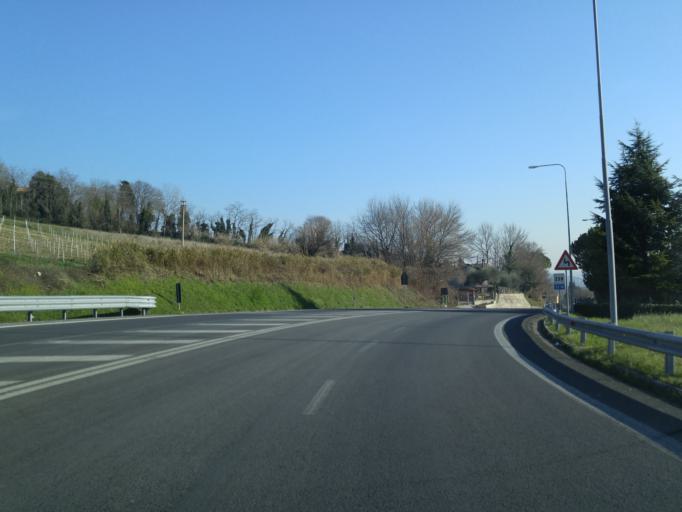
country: IT
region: The Marches
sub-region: Provincia di Pesaro e Urbino
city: Gradara
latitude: 43.9438
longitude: 12.8264
